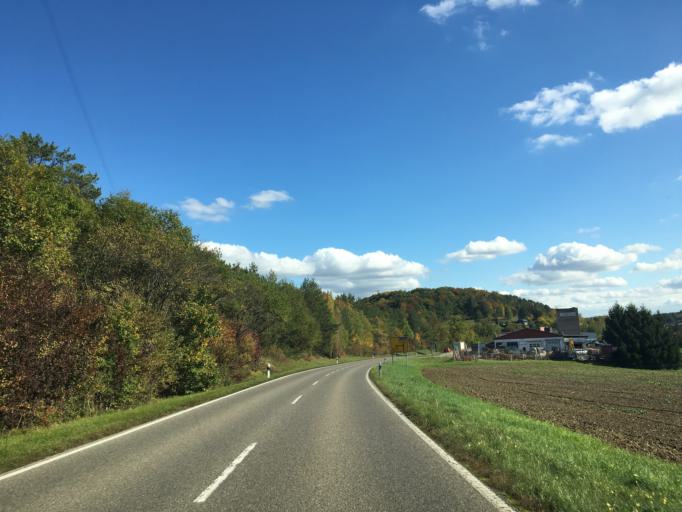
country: DE
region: Baden-Wuerttemberg
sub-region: Regierungsbezirk Stuttgart
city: Weil der Stadt
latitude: 48.7260
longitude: 8.8720
